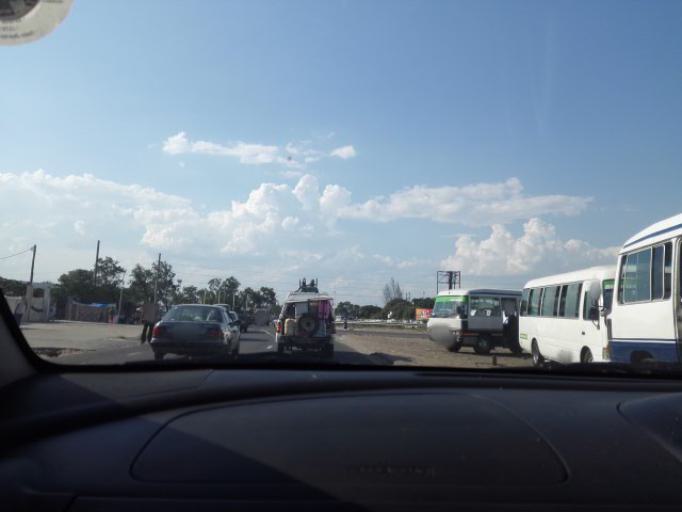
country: MZ
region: Maputo City
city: Maputo
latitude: -25.8774
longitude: 32.5667
